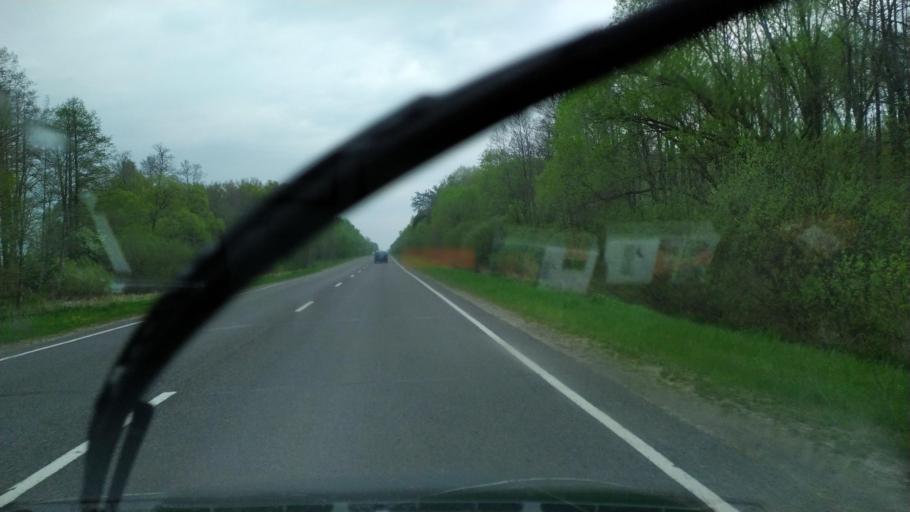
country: BY
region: Brest
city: Horad Kobryn
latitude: 52.3051
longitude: 24.5290
